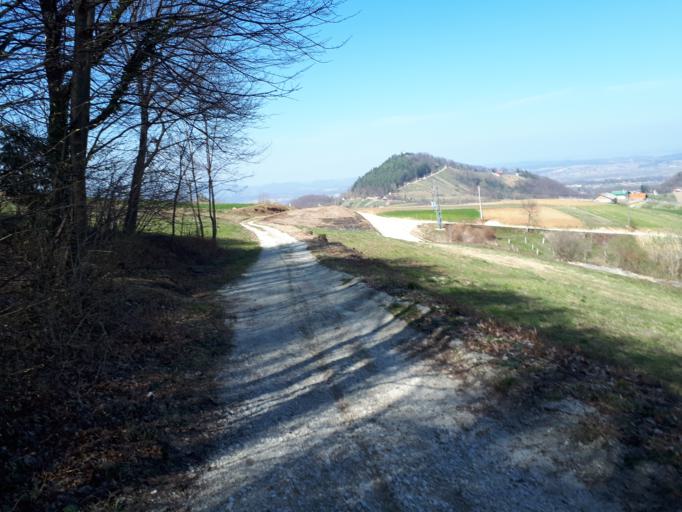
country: HR
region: Varazdinska
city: Ivanec
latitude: 46.1949
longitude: 16.1414
